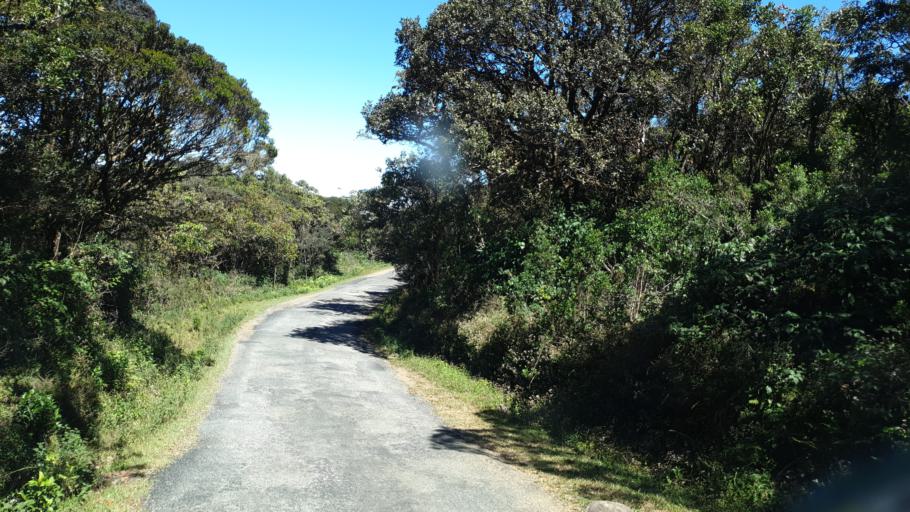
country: LK
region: Central
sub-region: Nuwara Eliya District
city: Nuwara Eliya
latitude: 6.8353
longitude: 80.8105
